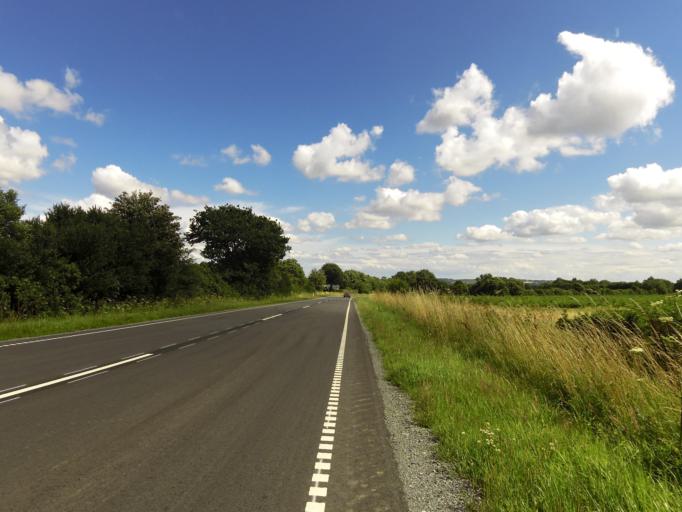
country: DK
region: South Denmark
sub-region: Haderslev Kommune
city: Gram
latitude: 55.3099
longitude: 9.1296
